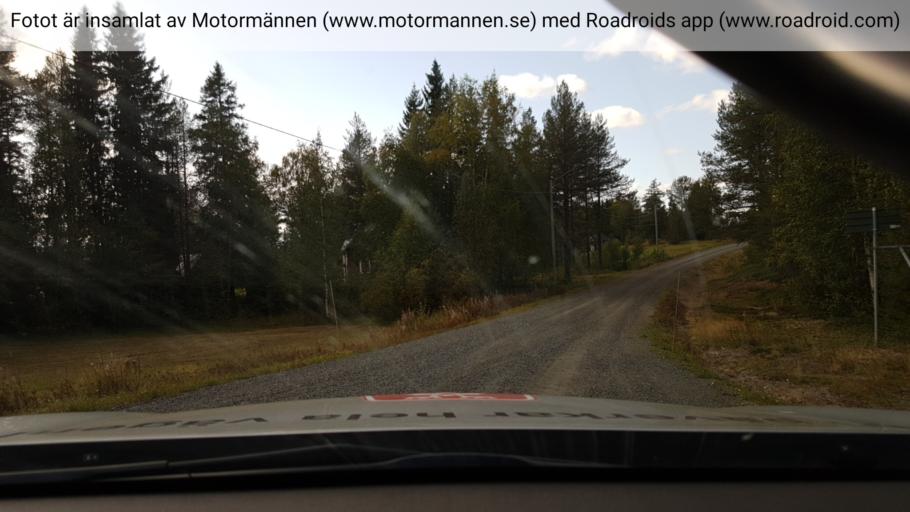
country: SE
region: Vaesterbotten
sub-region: Sorsele Kommun
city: Sorsele
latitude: 65.4613
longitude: 17.7779
